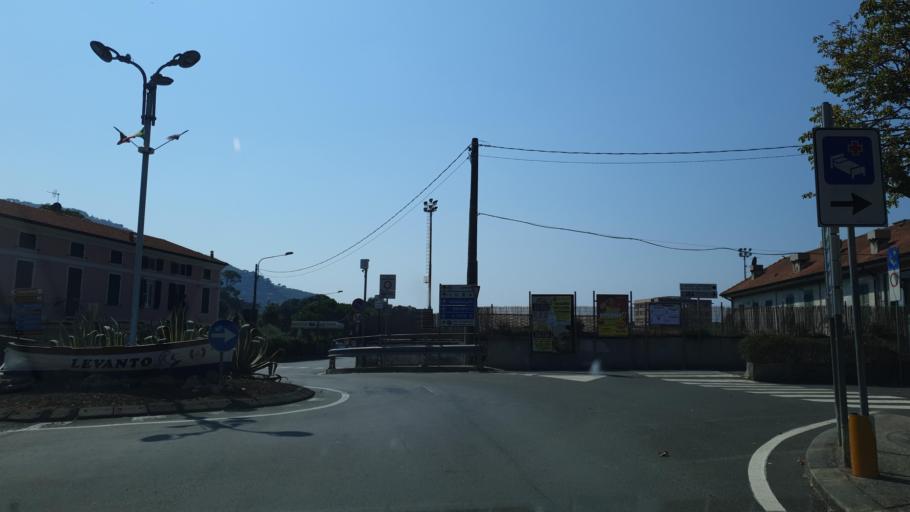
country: IT
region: Liguria
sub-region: Provincia di La Spezia
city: Levanto
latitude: 44.1757
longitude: 9.6194
